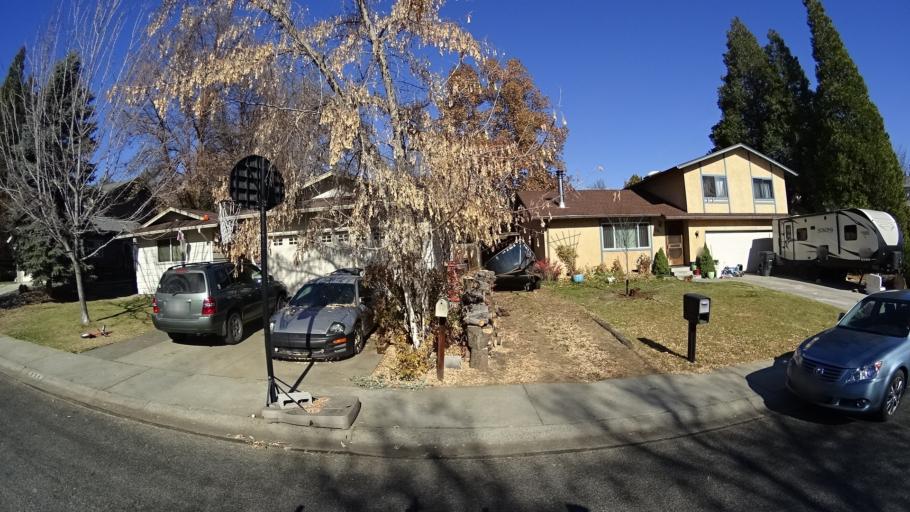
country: US
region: California
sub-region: Siskiyou County
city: Yreka
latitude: 41.7326
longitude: -122.6489
